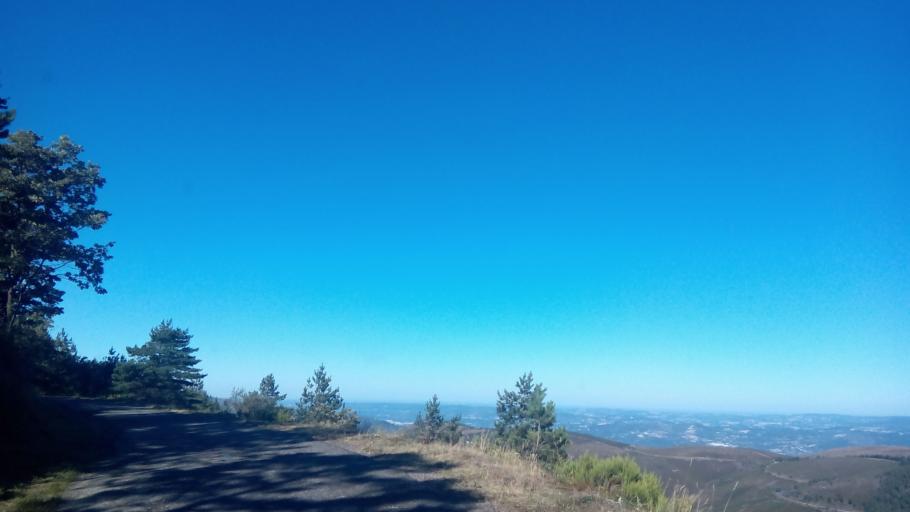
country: PT
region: Vila Real
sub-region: Mesao Frio
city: Mesao Frio
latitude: 41.2742
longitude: -7.9210
